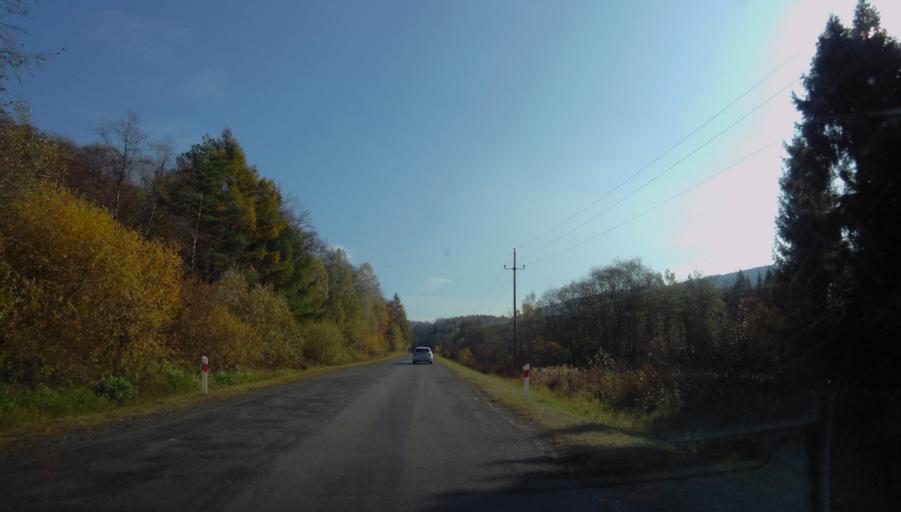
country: PL
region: Subcarpathian Voivodeship
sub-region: Powiat leski
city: Cisna
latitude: 49.2196
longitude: 22.2082
